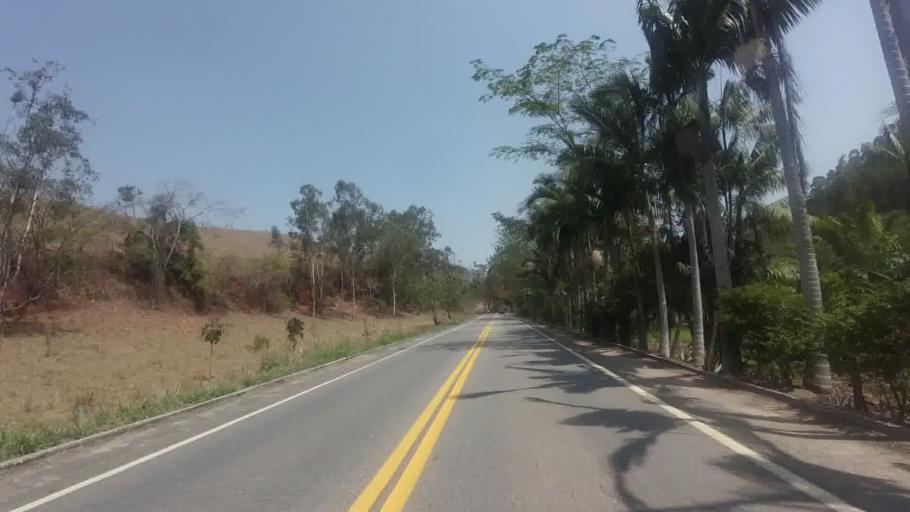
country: BR
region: Espirito Santo
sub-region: Mimoso Do Sul
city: Mimoso do Sul
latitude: -20.9254
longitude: -41.3176
